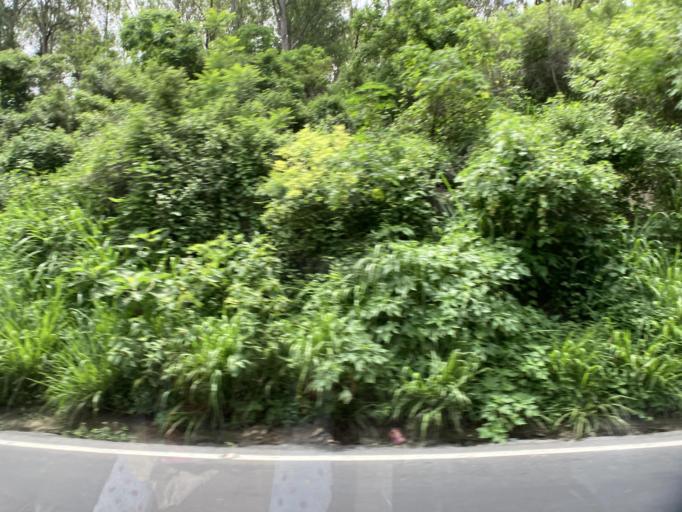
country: GT
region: Guatemala
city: Amatitlan
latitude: 14.4979
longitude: -90.6254
